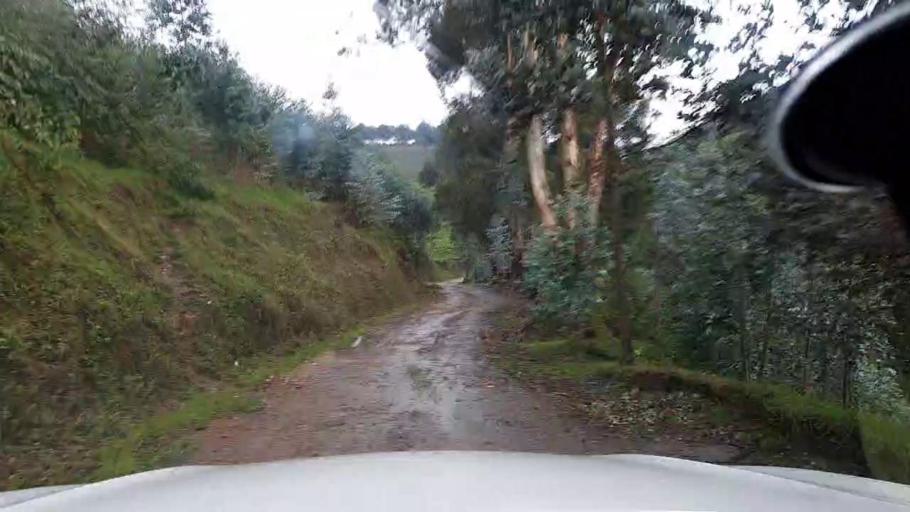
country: RW
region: Western Province
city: Kibuye
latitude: -2.0793
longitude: 29.5149
